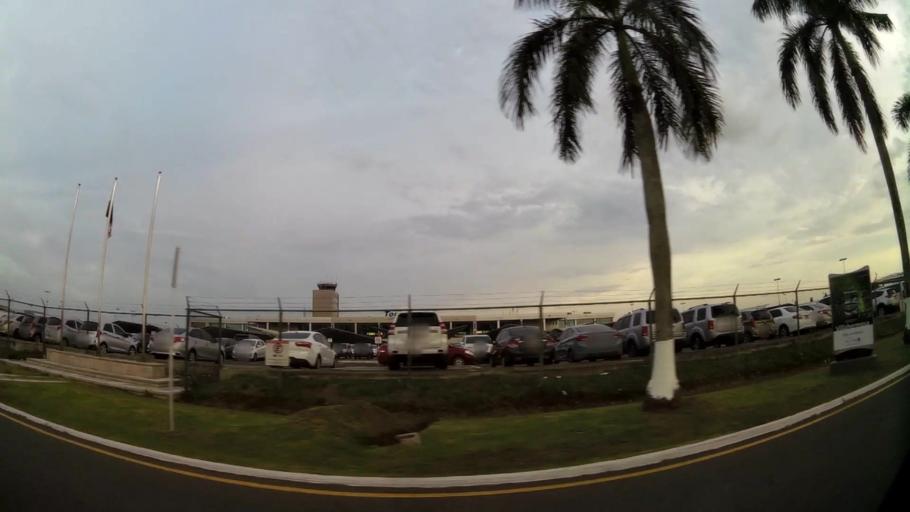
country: PA
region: Panama
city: Tocumen
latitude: 9.0680
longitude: -79.3888
